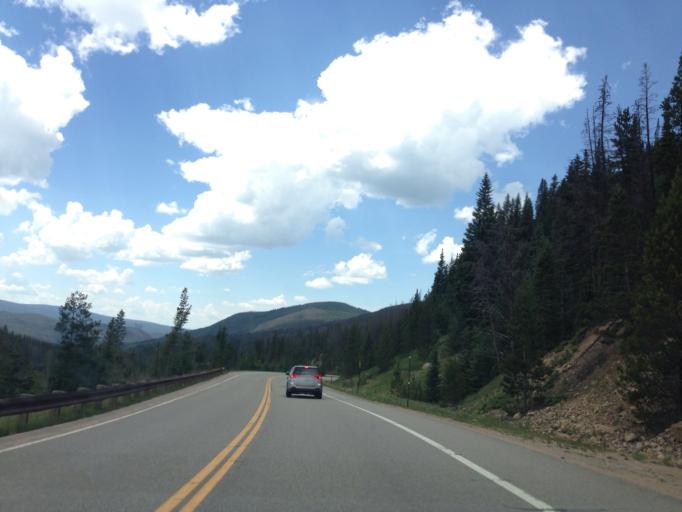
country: US
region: Colorado
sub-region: Larimer County
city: Estes Park
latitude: 40.5043
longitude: -105.9039
